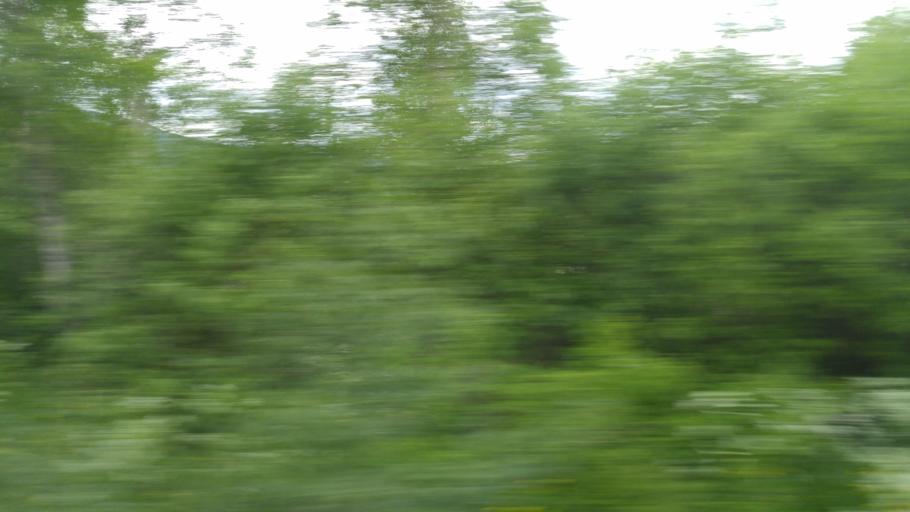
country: NO
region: Nord-Trondelag
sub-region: Meraker
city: Meraker
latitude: 63.4215
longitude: 11.7593
